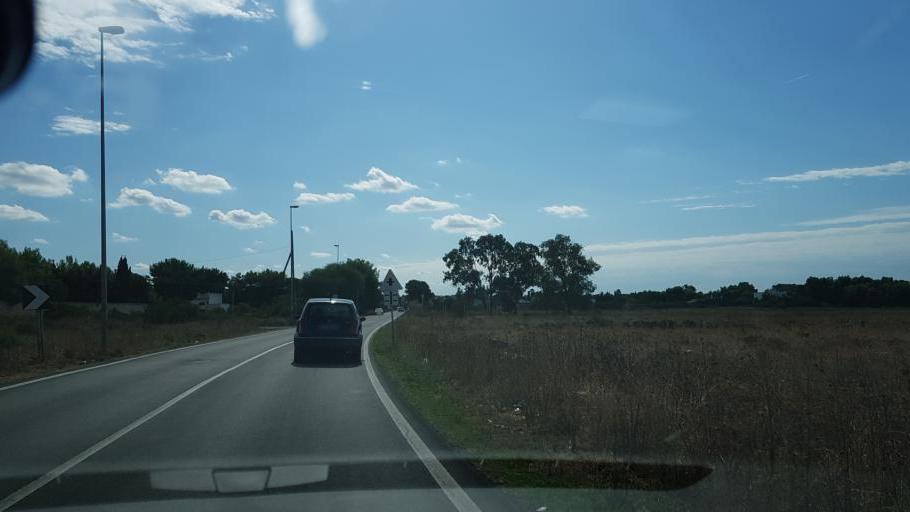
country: IT
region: Apulia
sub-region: Provincia di Lecce
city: Porto Cesareo
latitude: 40.2504
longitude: 17.9109
